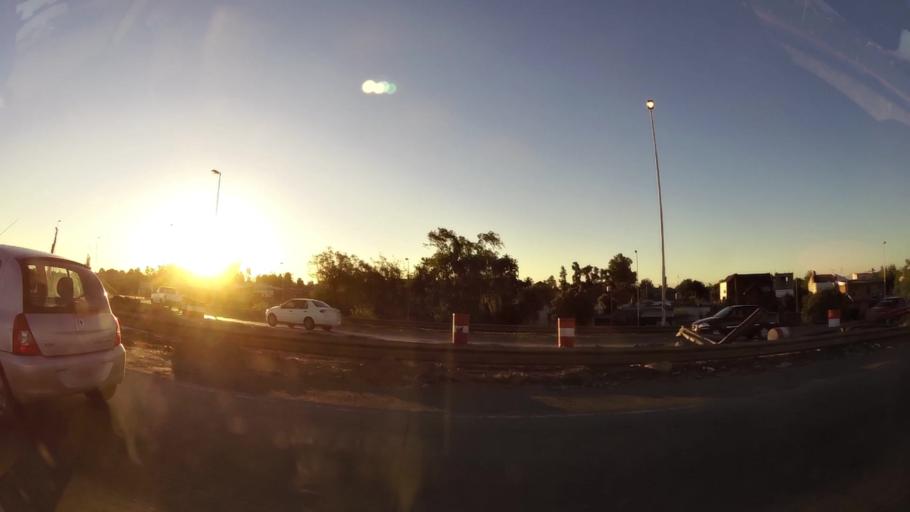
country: AR
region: Buenos Aires
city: Pontevedra
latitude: -34.7580
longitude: -58.6154
